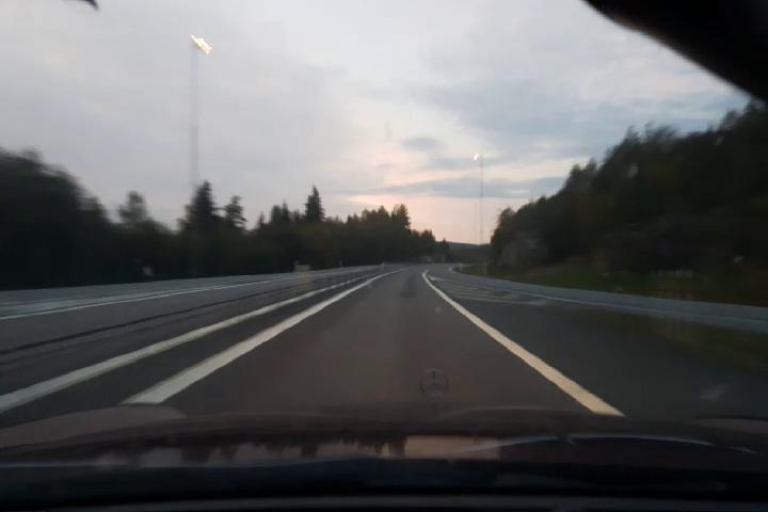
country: SE
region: Vaesternorrland
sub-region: Kramfors Kommun
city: Nordingra
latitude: 62.9408
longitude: 18.0941
